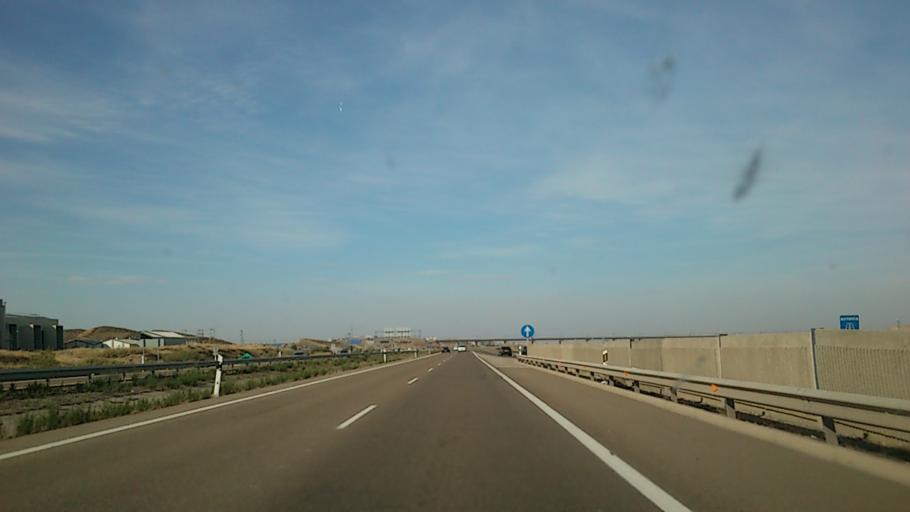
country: ES
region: Aragon
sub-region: Provincia de Zaragoza
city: Cuarte de Huerva
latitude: 41.5955
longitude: -0.9418
